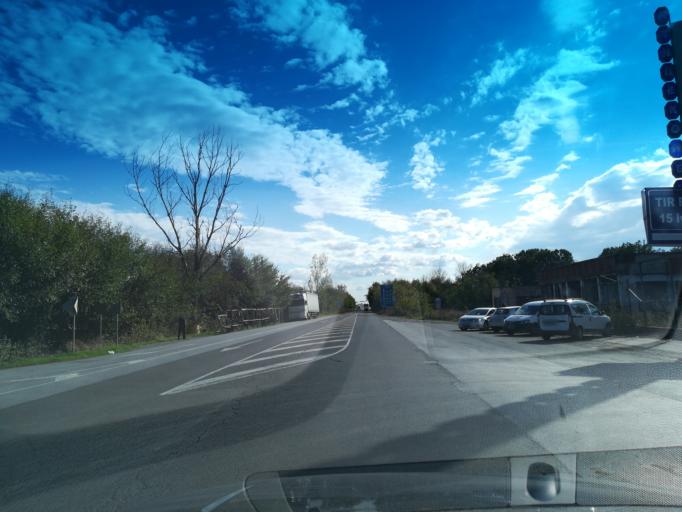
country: BG
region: Stara Zagora
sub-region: Obshtina Stara Zagora
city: Stara Zagora
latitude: 42.3492
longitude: 25.6591
